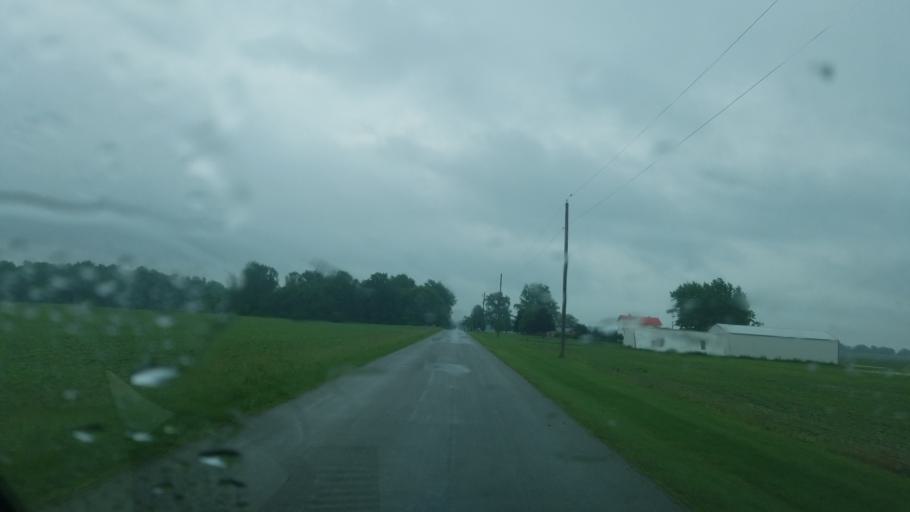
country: US
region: Ohio
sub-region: Huron County
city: Plymouth
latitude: 40.9453
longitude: -82.7558
